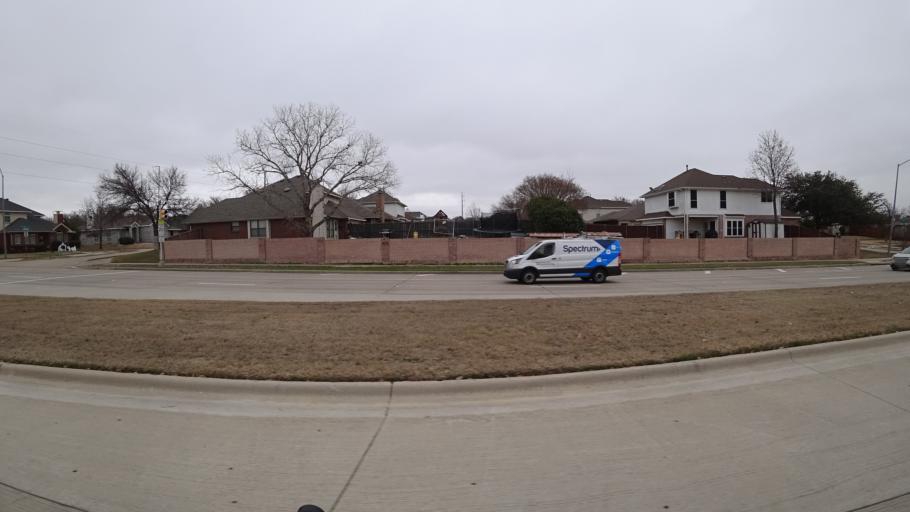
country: US
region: Texas
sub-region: Denton County
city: Lewisville
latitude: 33.0316
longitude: -97.0362
